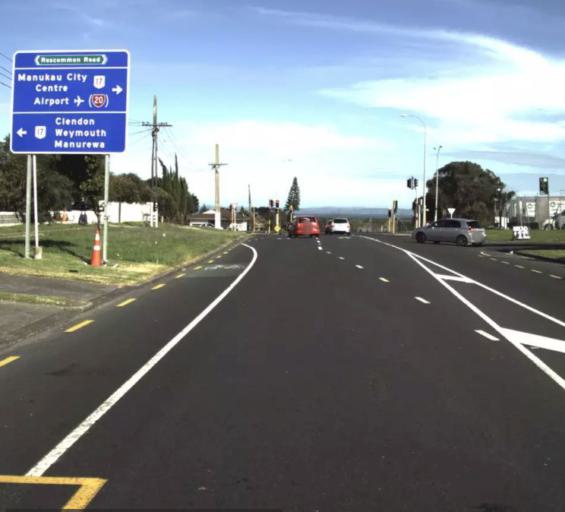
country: NZ
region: Auckland
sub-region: Auckland
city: Wiri
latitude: -37.0185
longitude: 174.8634
